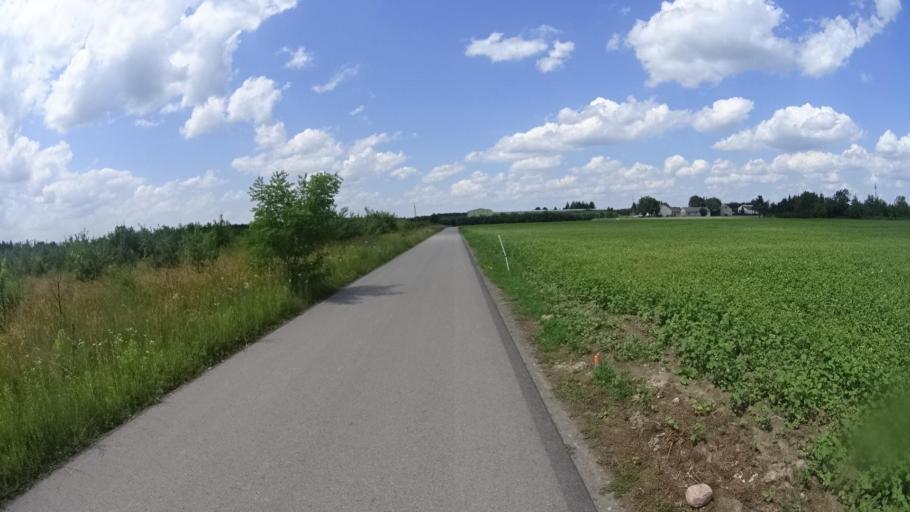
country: PL
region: Masovian Voivodeship
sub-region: Powiat bialobrzeski
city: Promna
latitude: 51.7047
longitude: 20.9211
